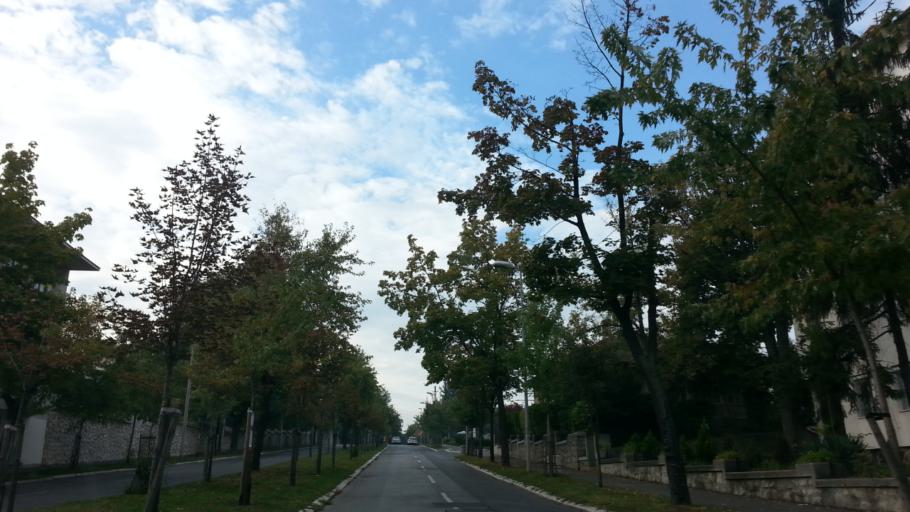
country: RS
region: Central Serbia
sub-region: Belgrade
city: Savski Venac
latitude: 44.7732
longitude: 20.4550
